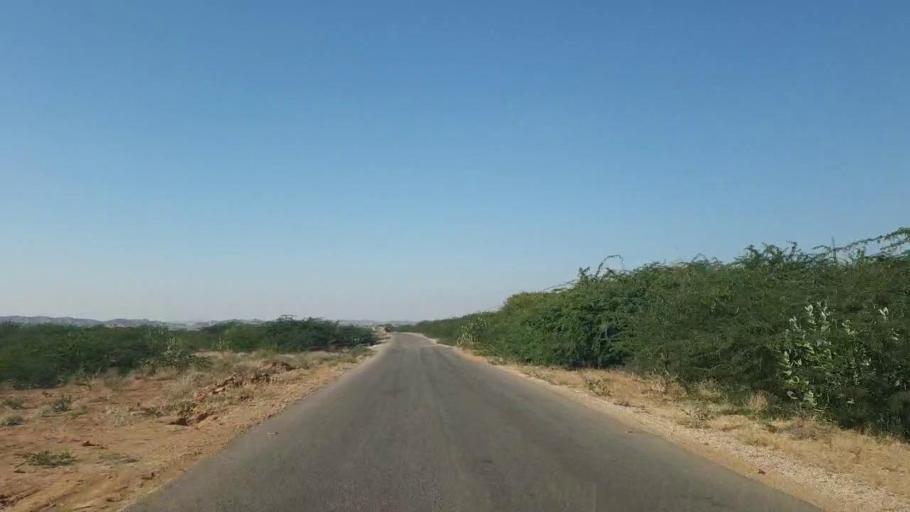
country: PK
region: Sindh
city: Malir Cantonment
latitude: 25.2755
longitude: 67.5890
